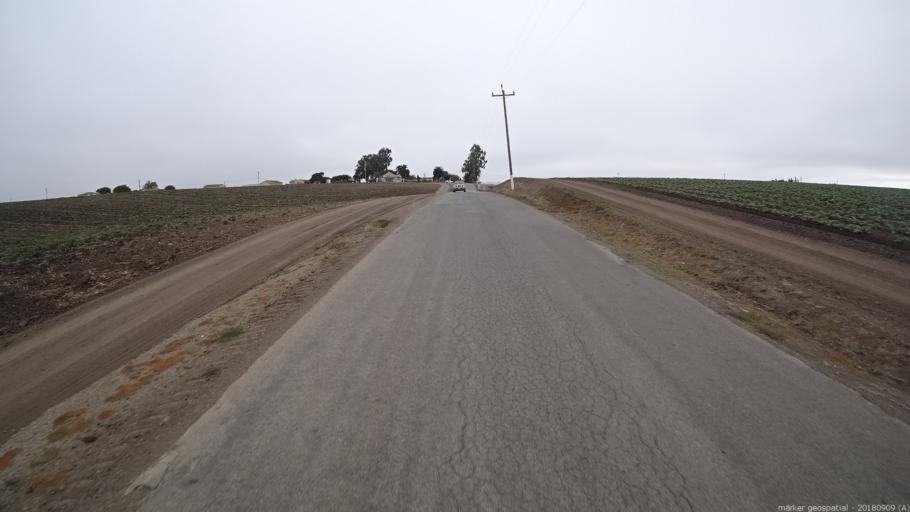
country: US
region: California
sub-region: Monterey County
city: Boronda
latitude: 36.7199
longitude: -121.6969
